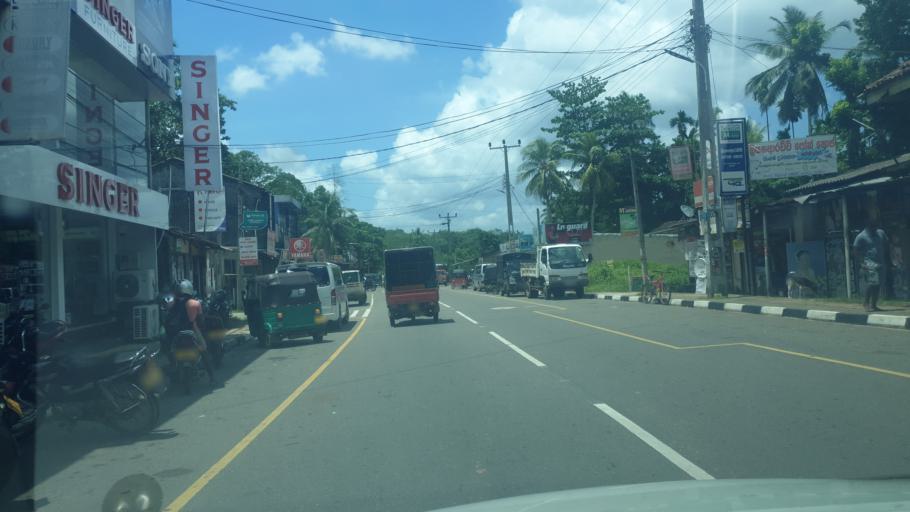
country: LK
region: Western
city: Horawala Junction
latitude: 6.5160
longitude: 80.2341
